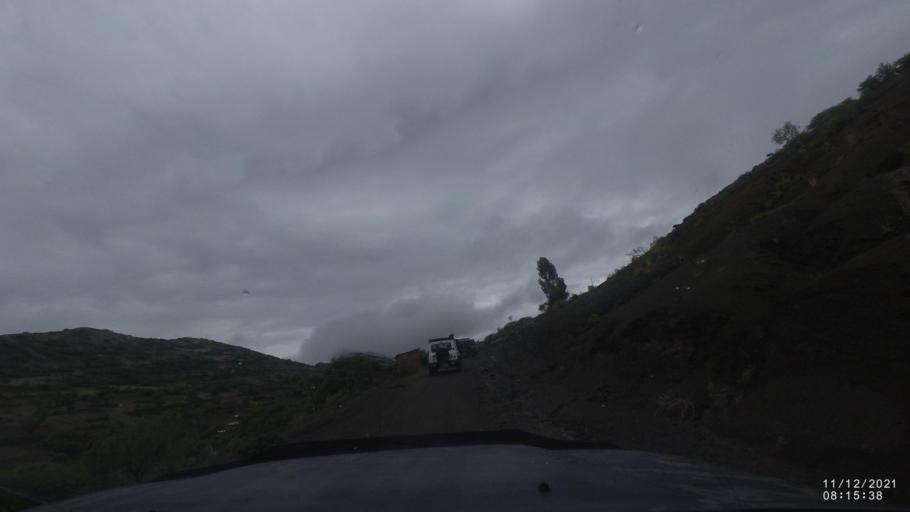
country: BO
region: Cochabamba
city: Tarata
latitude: -17.9448
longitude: -65.9278
